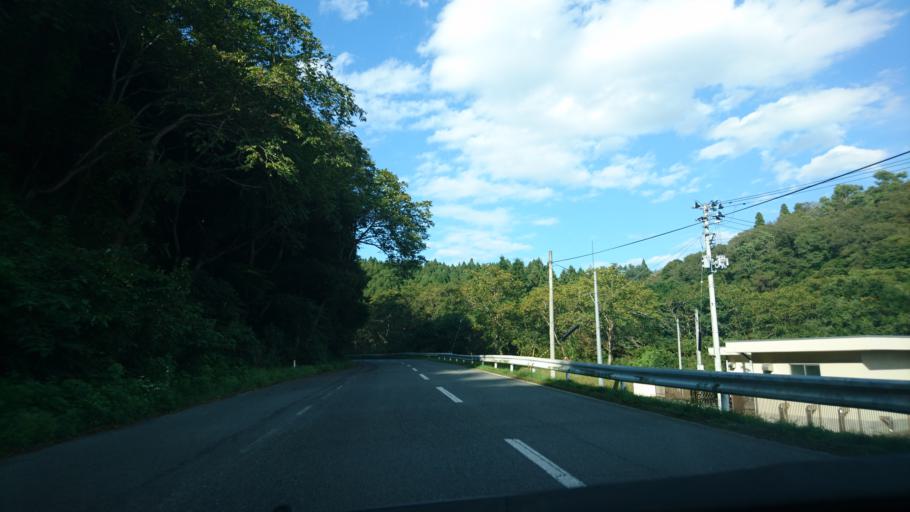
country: JP
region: Iwate
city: Ichinoseki
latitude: 38.8545
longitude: 141.3030
